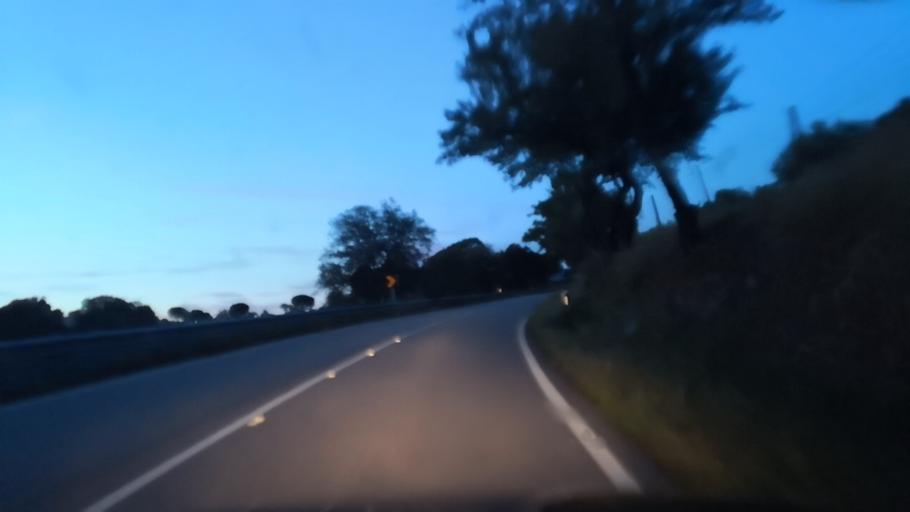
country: ES
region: Extremadura
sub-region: Provincia de Caceres
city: Piedras Albas
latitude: 39.8379
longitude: -6.9755
